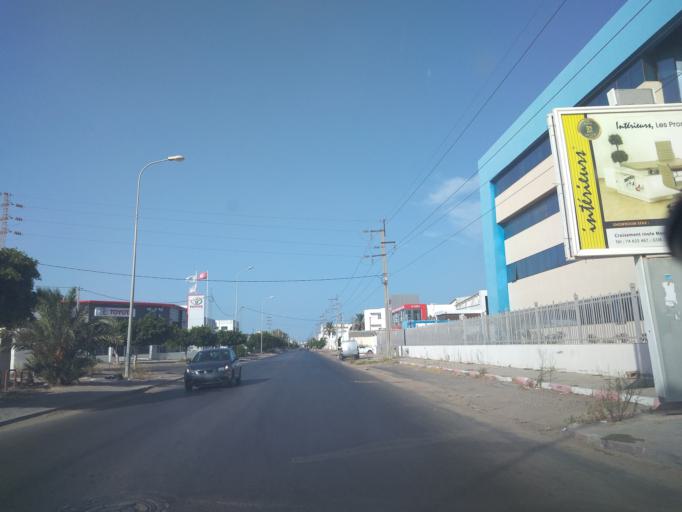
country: TN
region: Safaqis
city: Al Qarmadah
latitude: 34.7483
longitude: 10.7726
